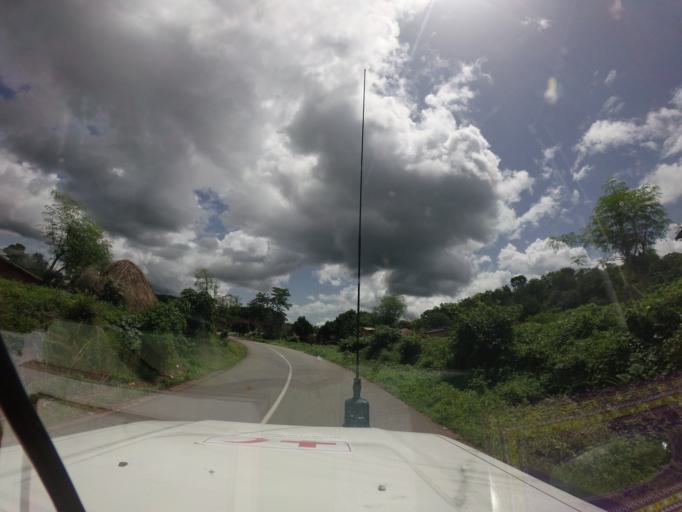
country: SL
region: Northern Province
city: Bindi
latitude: 10.1652
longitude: -11.5047
